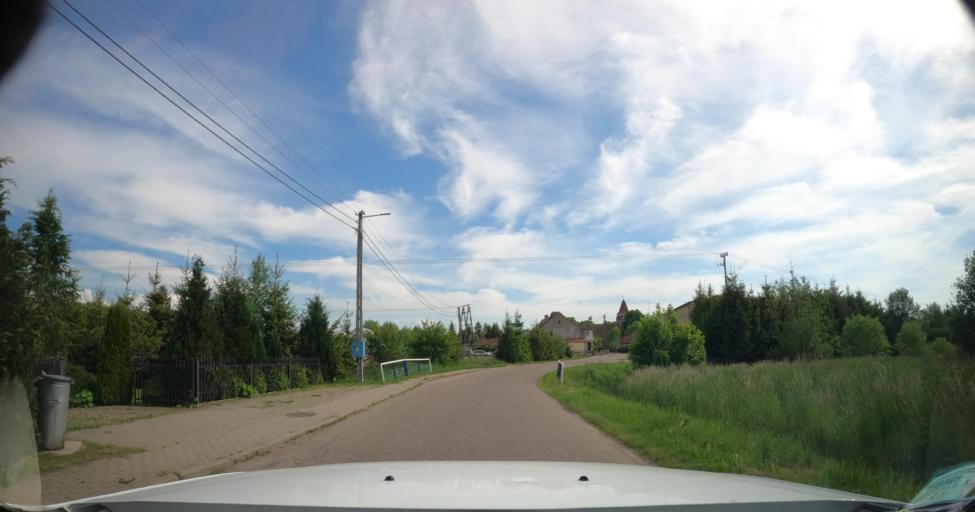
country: PL
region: Warmian-Masurian Voivodeship
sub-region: Powiat lidzbarski
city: Lubomino
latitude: 54.0699
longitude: 20.2394
